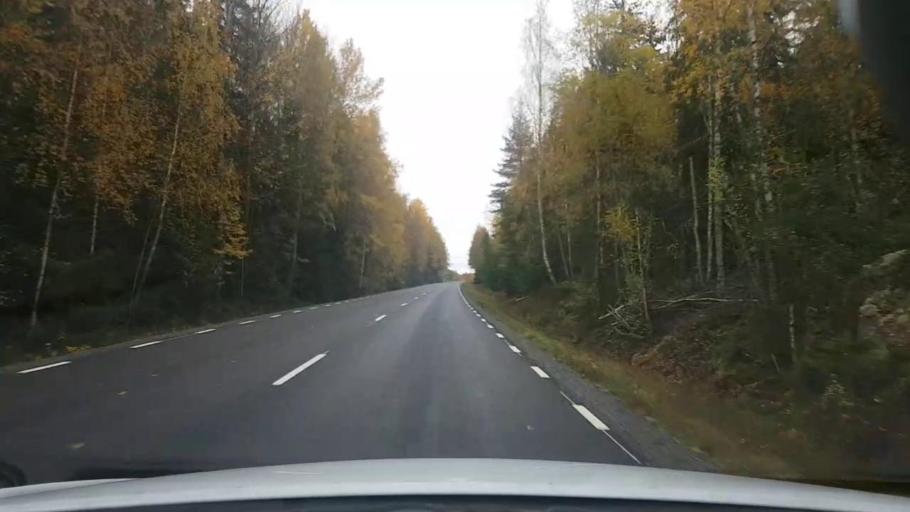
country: SE
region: OErebro
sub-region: Laxa Kommun
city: Laxa
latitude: 58.8047
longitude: 14.5433
